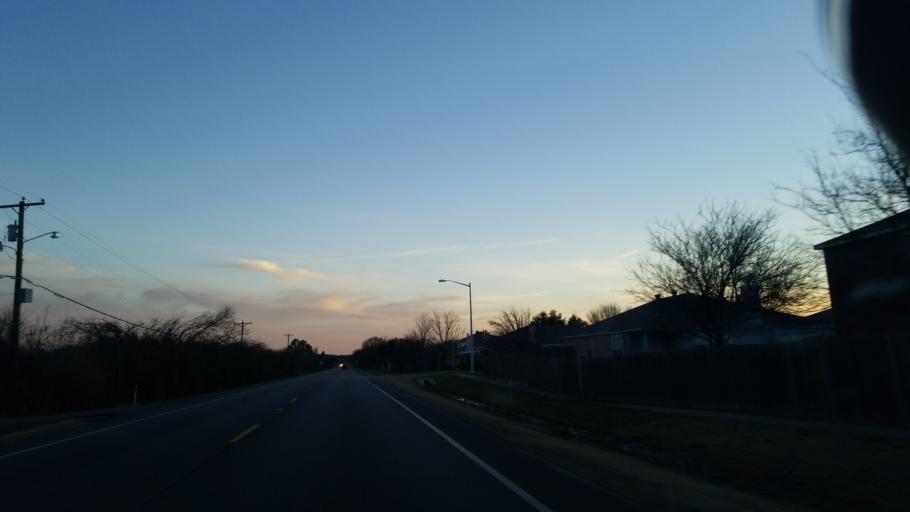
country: US
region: Texas
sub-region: Denton County
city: Denton
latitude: 33.1687
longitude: -97.1419
